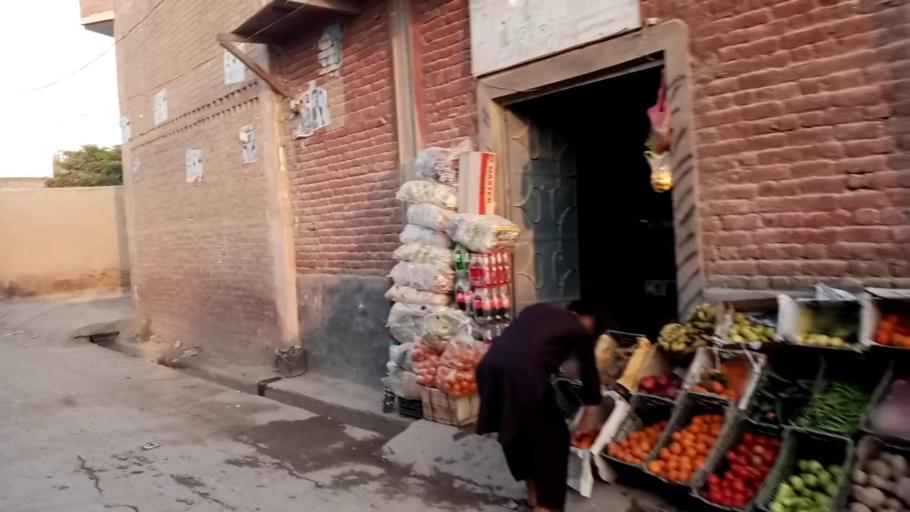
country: PK
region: Khyber Pakhtunkhwa
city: Peshawar
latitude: 34.0471
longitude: 71.4543
